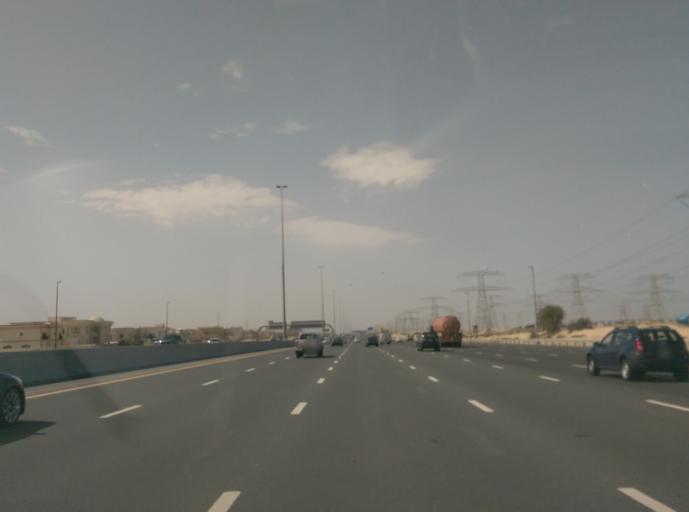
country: AE
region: Dubai
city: Dubai
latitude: 25.0945
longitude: 55.2261
